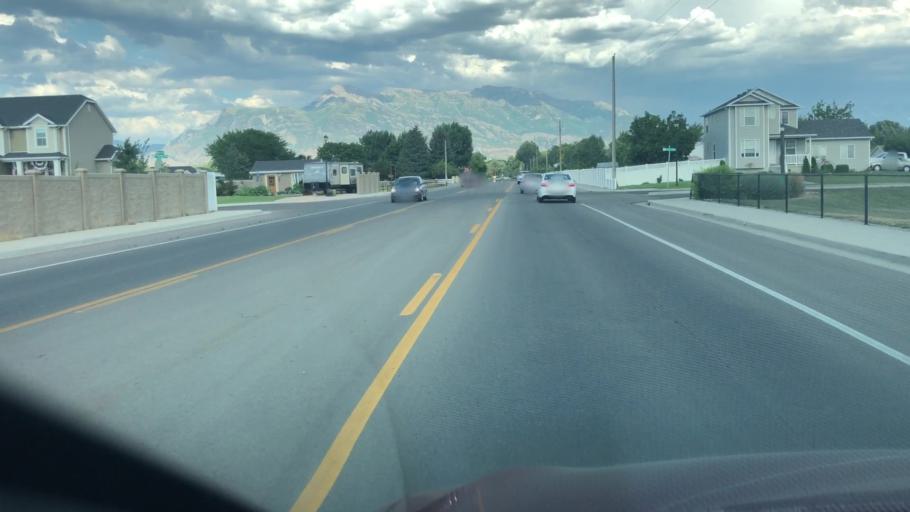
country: US
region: Utah
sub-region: Utah County
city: Lehi
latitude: 40.3872
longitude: -111.8740
